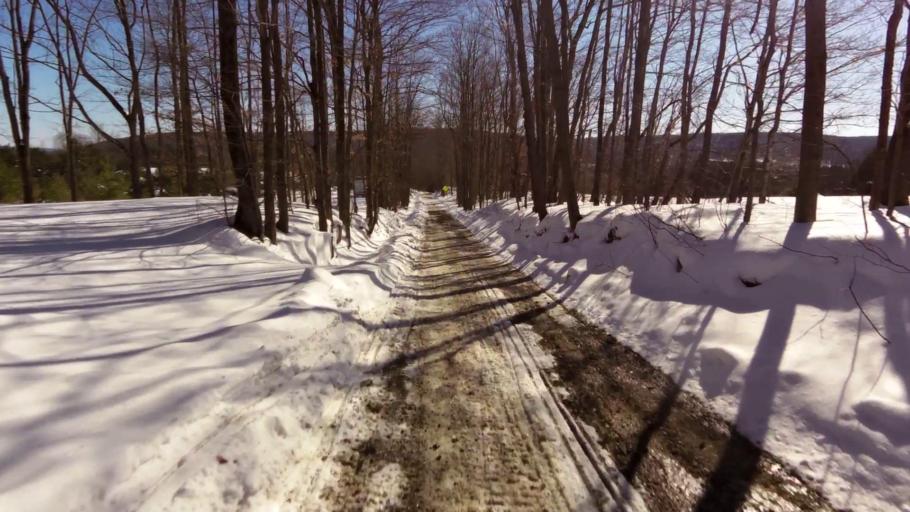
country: US
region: New York
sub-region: Allegany County
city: Cuba
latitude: 42.3489
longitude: -78.3173
